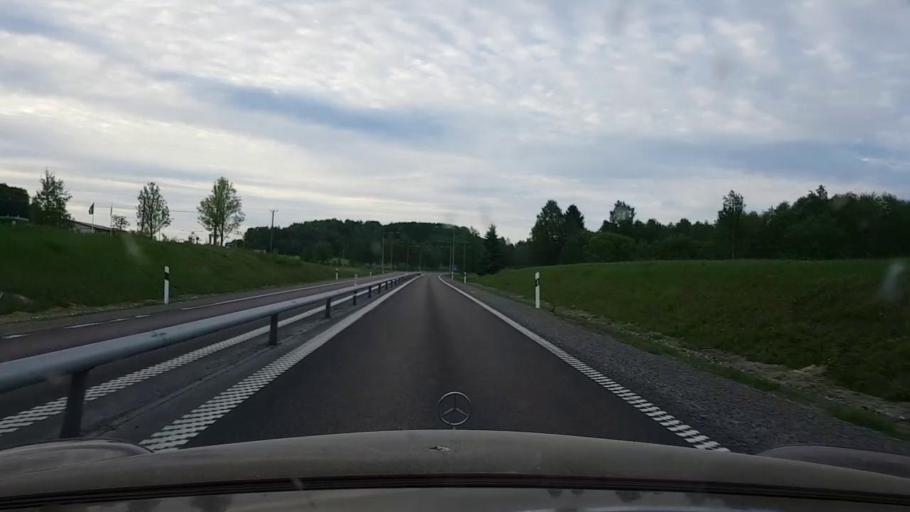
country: SE
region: OErebro
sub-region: Askersunds Kommun
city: Askersund
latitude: 58.8860
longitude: 14.8993
